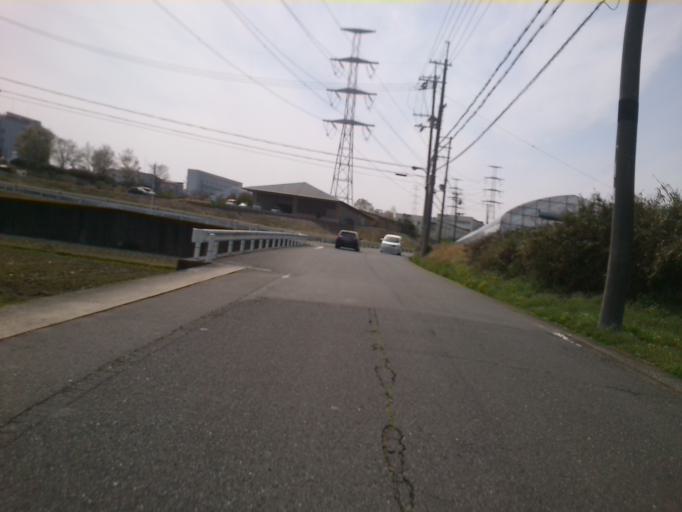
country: JP
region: Kyoto
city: Tanabe
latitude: 34.7485
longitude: 135.7610
